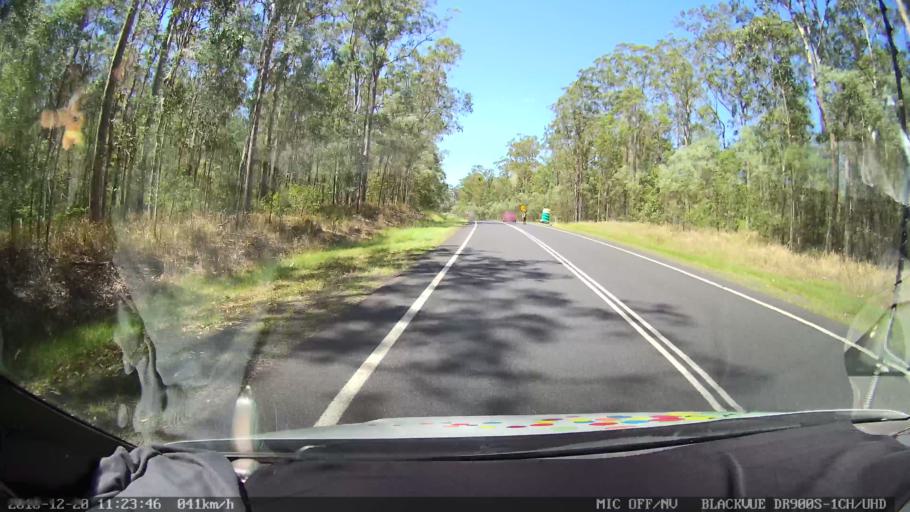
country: AU
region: New South Wales
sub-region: Richmond Valley
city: Casino
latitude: -29.0674
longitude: 153.0037
